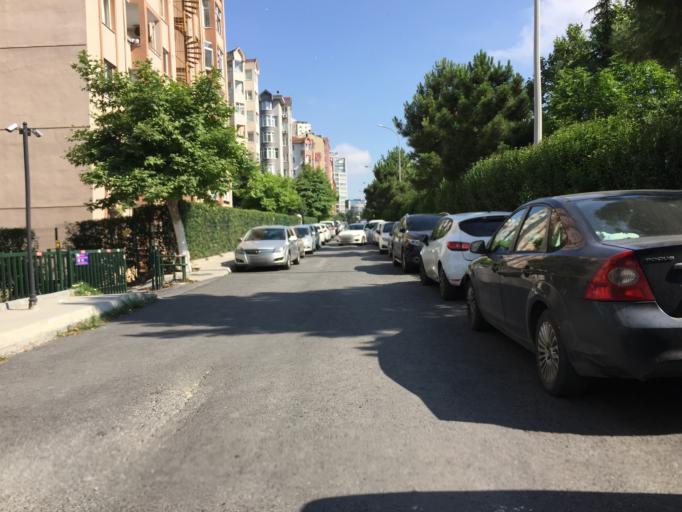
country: TR
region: Istanbul
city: Esenyurt
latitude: 41.0617
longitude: 28.6717
